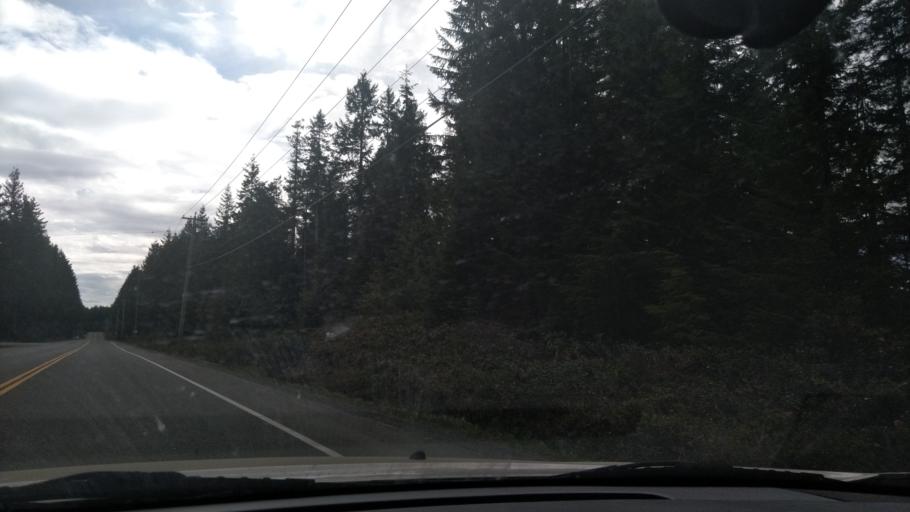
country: CA
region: British Columbia
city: Campbell River
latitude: 50.0170
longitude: -125.3544
